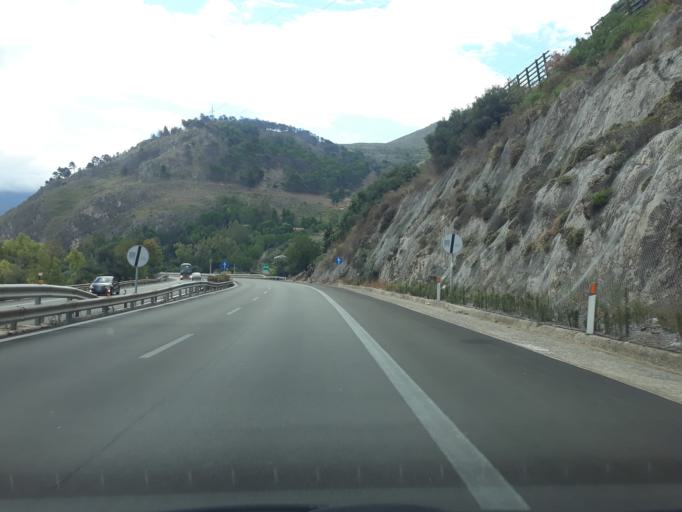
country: IT
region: Sicily
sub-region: Palermo
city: Trabia
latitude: 37.9884
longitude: 13.6552
